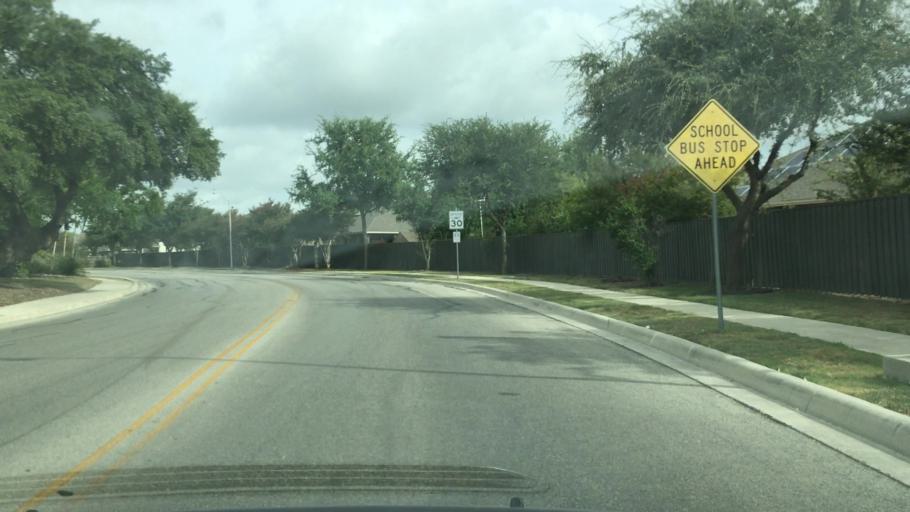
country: US
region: Texas
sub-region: Guadalupe County
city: Cibolo
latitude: 29.5758
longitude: -98.2365
